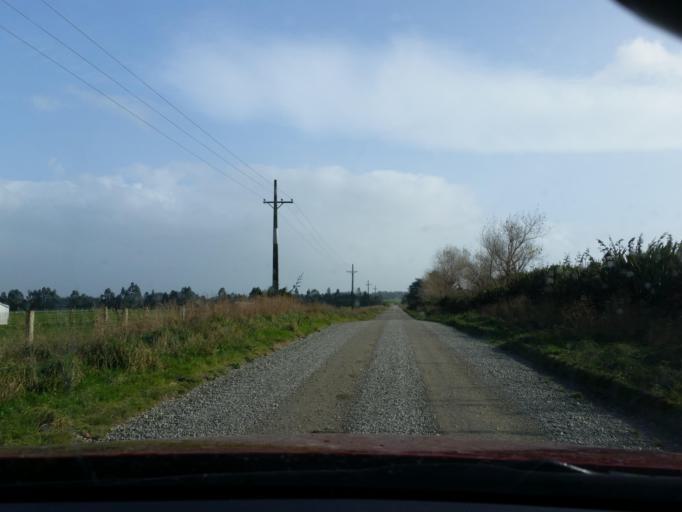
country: NZ
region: Southland
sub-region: Invercargill City
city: Invercargill
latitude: -46.2916
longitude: 168.4242
